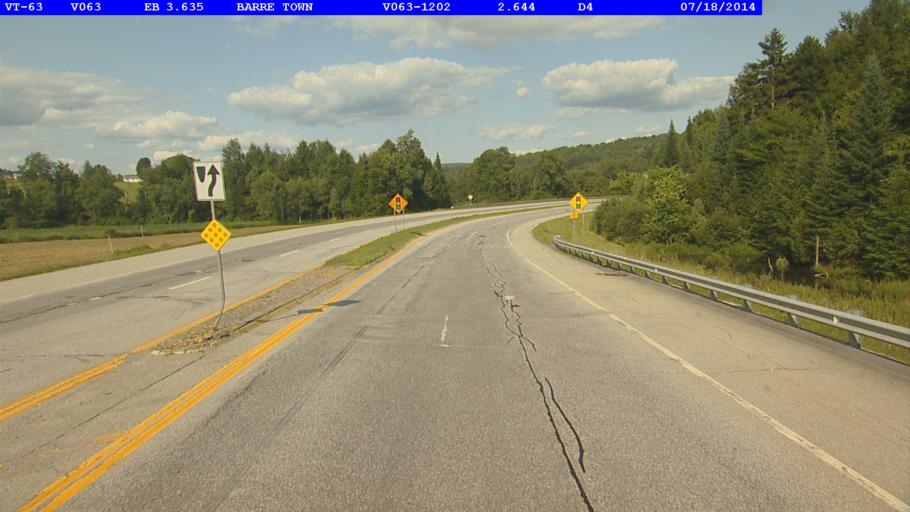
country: US
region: Vermont
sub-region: Washington County
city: South Barre
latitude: 44.1738
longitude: -72.5125
